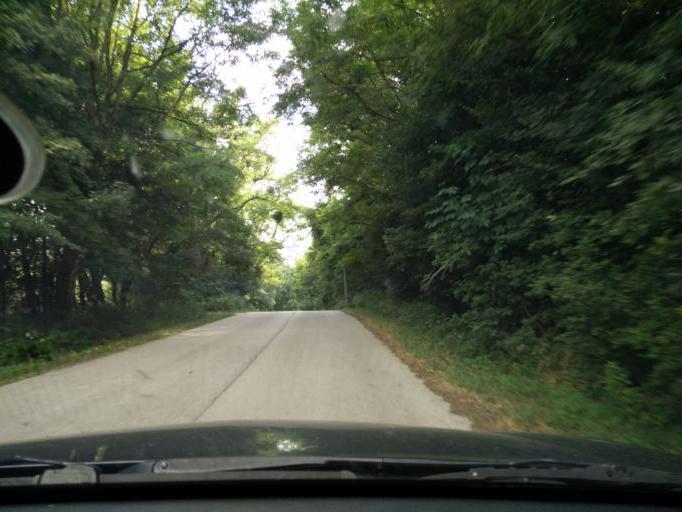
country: HU
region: Komarom-Esztergom
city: Tardos
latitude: 47.7083
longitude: 18.4504
